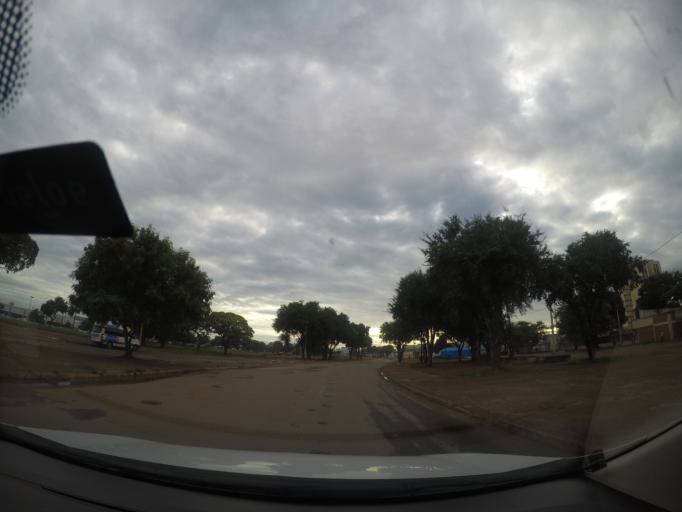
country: BR
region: Goias
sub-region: Goiania
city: Goiania
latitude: -16.6635
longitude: -49.2607
